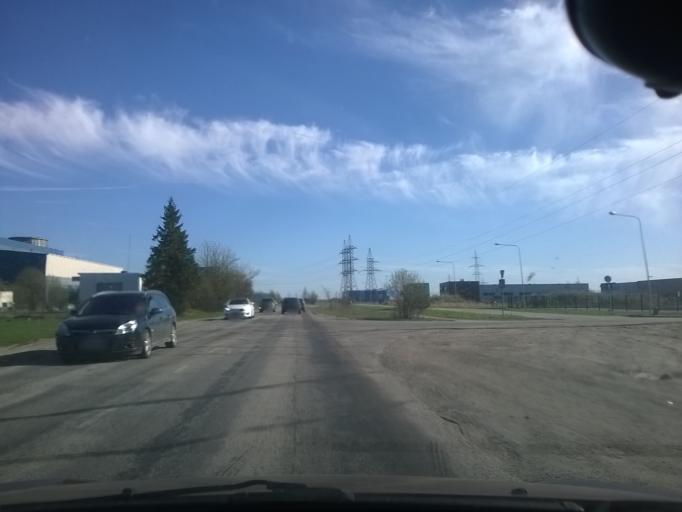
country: EE
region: Harju
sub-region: Joelaehtme vald
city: Loo
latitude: 59.4548
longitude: 24.9196
